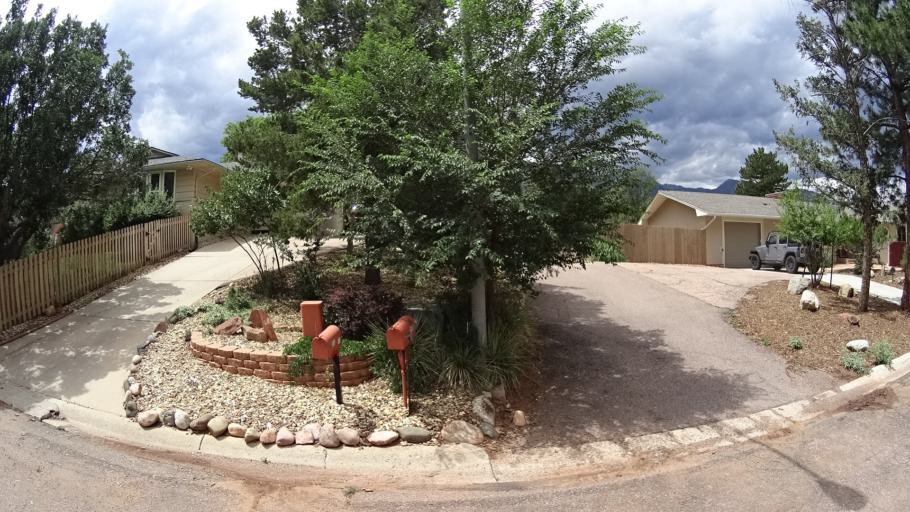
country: US
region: Colorado
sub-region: El Paso County
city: Manitou Springs
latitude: 38.8515
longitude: -104.8927
